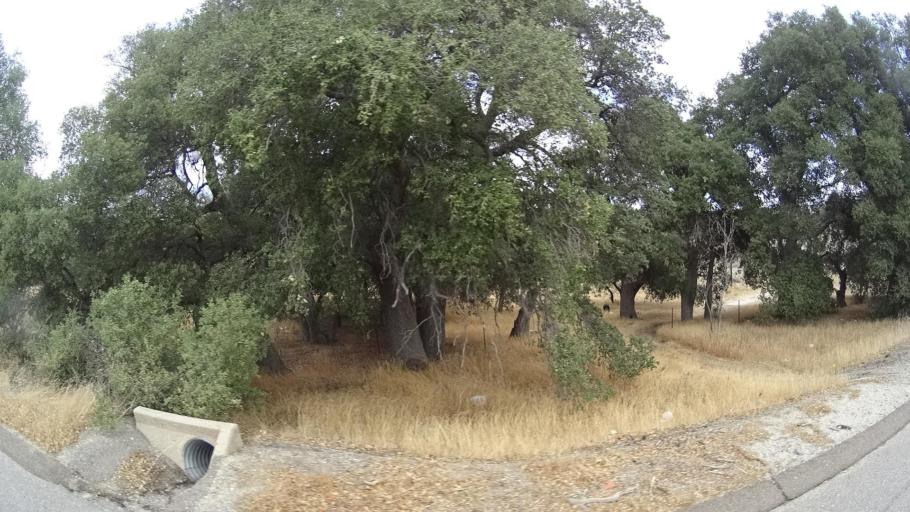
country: US
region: California
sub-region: San Diego County
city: Campo
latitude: 32.6948
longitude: -116.3451
